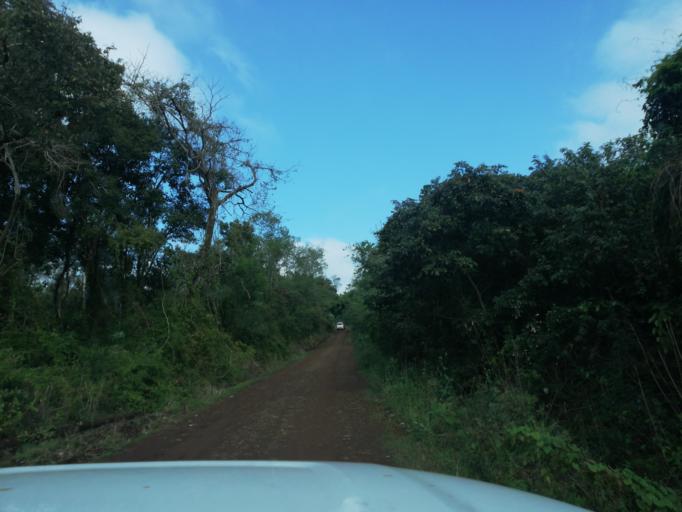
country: AR
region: Misiones
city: Cerro Azul
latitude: -27.5759
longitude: -55.5067
